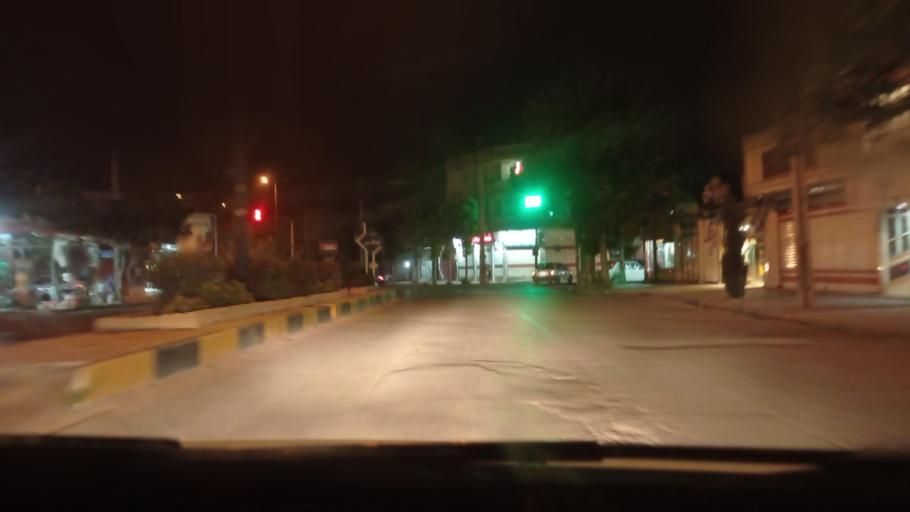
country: IR
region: Lorestan
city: Kuhdasht
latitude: 33.5386
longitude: 47.6103
